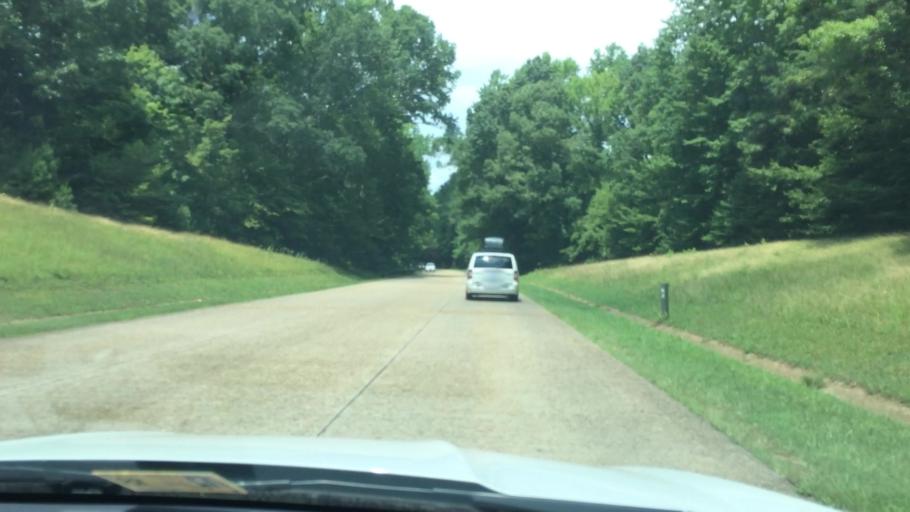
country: US
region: Virginia
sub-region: York County
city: Yorktown
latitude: 37.2367
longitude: -76.5223
